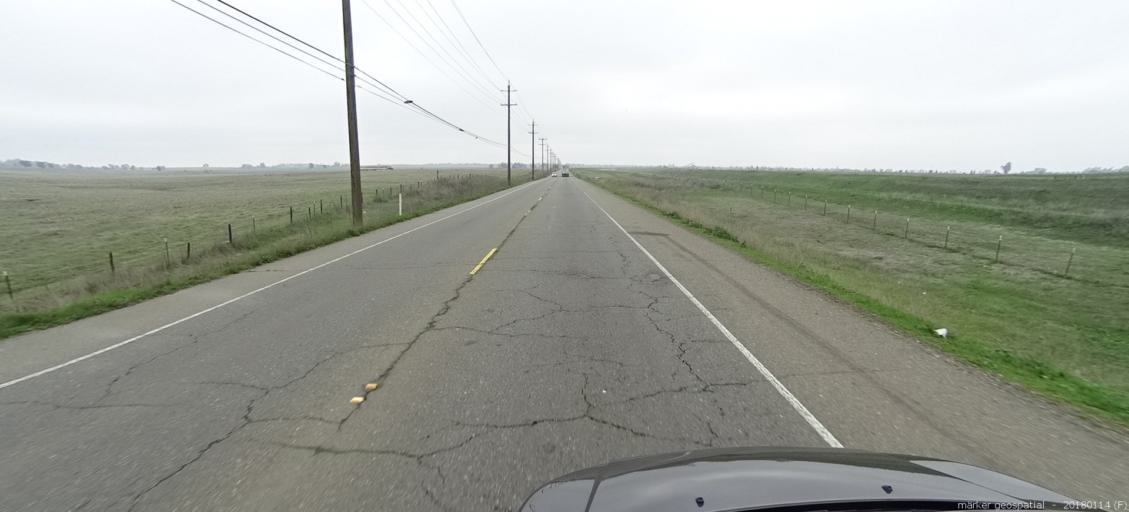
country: US
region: California
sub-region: Sacramento County
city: Rancho Cordova
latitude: 38.5200
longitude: -121.2427
